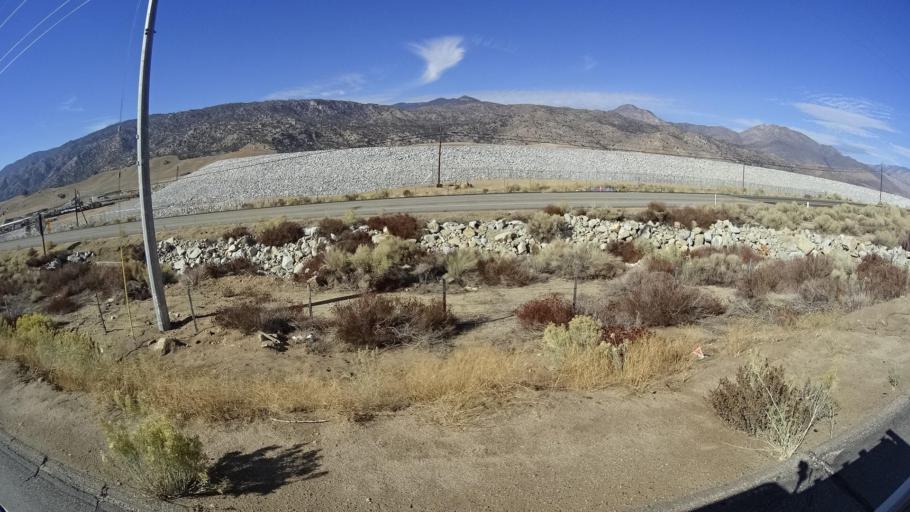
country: US
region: California
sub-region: Kern County
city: Lake Isabella
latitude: 35.6446
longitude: -118.4619
